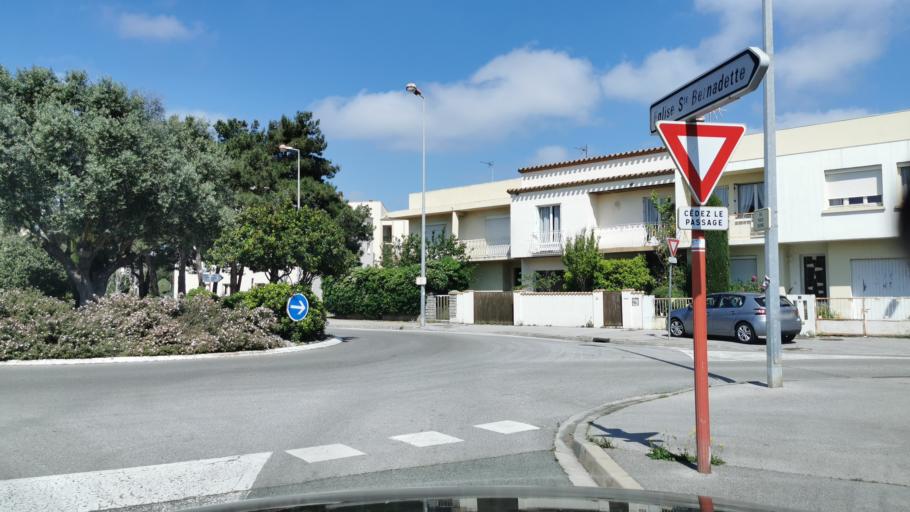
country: FR
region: Languedoc-Roussillon
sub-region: Departement de l'Aude
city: Narbonne
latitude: 43.1850
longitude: 3.0158
